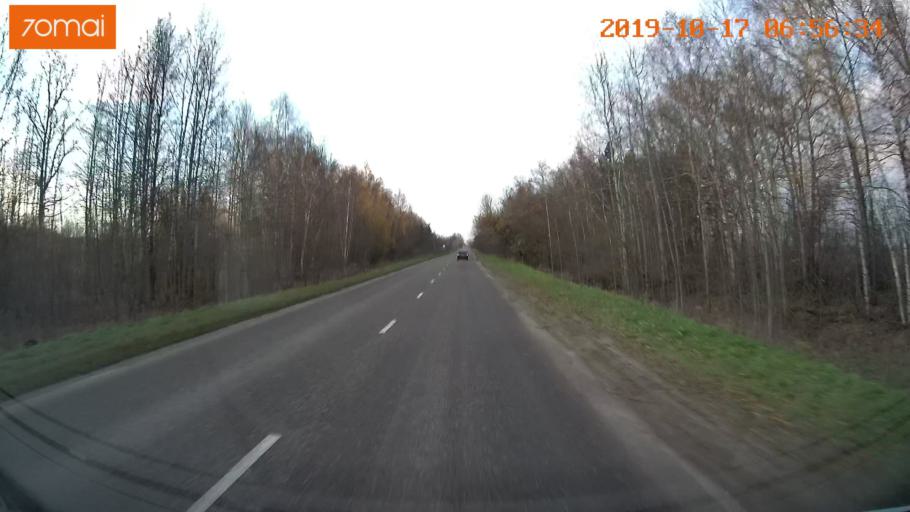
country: RU
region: Vladimir
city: Suzdal'
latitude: 56.4452
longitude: 40.4466
